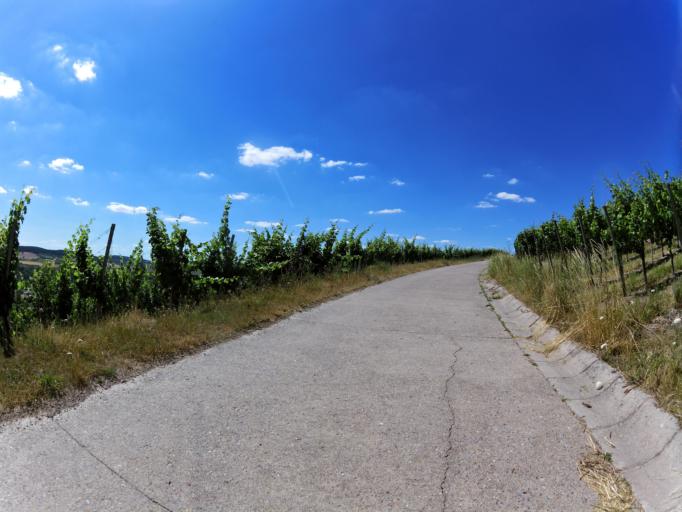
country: DE
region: Bavaria
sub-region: Regierungsbezirk Unterfranken
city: Thungersheim
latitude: 49.8886
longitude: 9.8491
